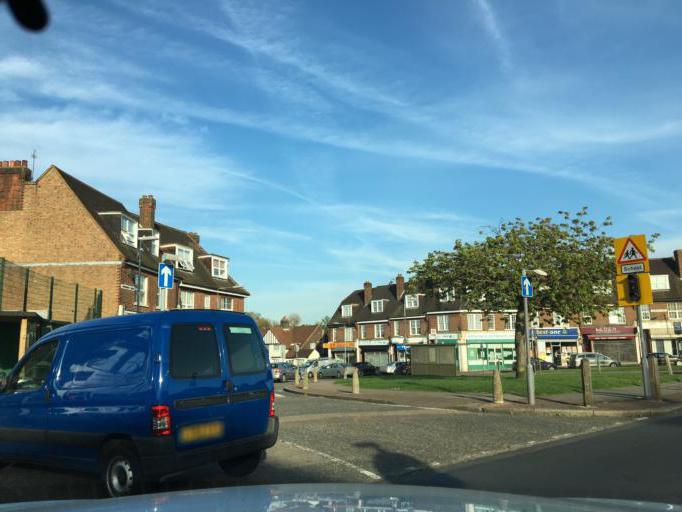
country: GB
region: England
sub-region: Greater London
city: Blackheath
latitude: 51.4456
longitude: 0.0397
